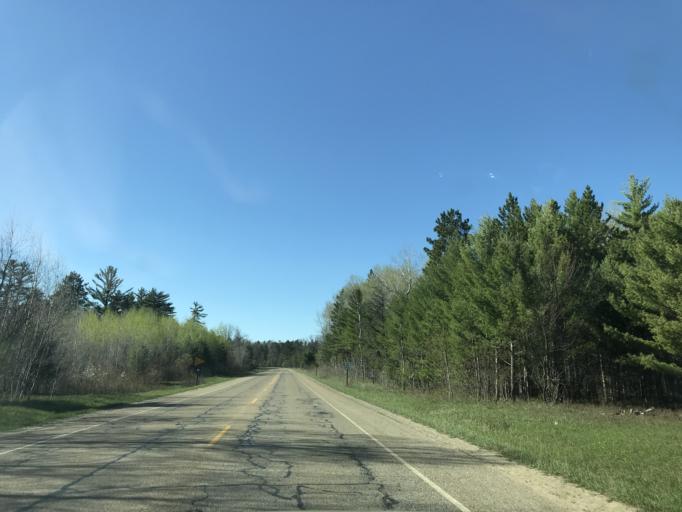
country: US
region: Michigan
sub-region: Crawford County
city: Grayling
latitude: 44.7172
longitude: -84.7443
